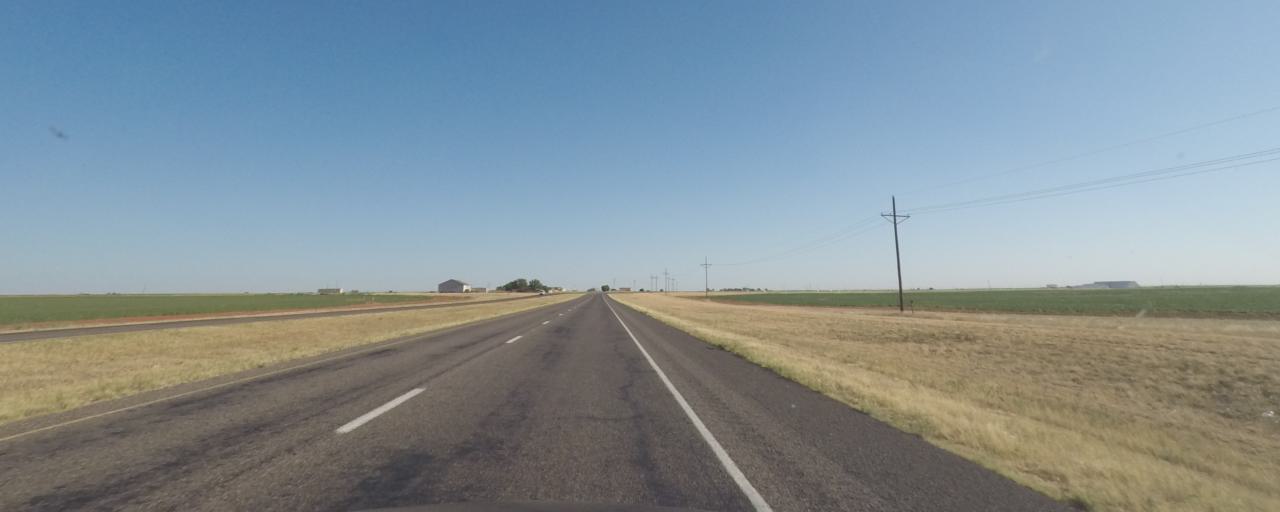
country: US
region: Texas
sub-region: Gaines County
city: Seagraves
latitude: 32.8658
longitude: -102.6401
